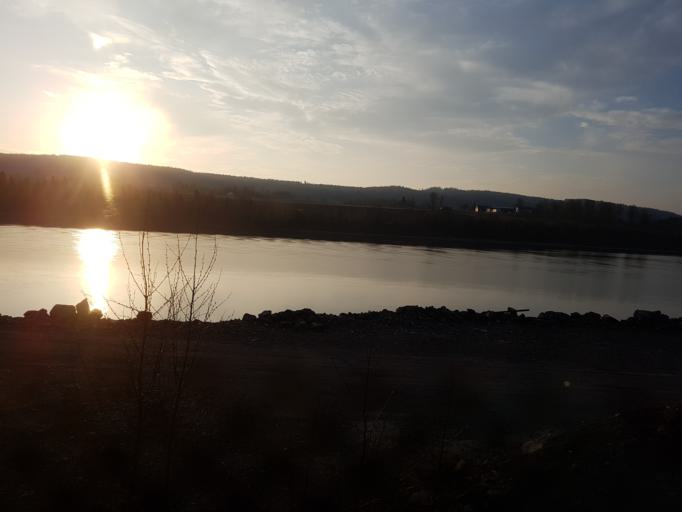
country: NO
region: Akershus
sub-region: Eidsvoll
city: Eidsvoll
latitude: 60.3544
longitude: 11.2454
